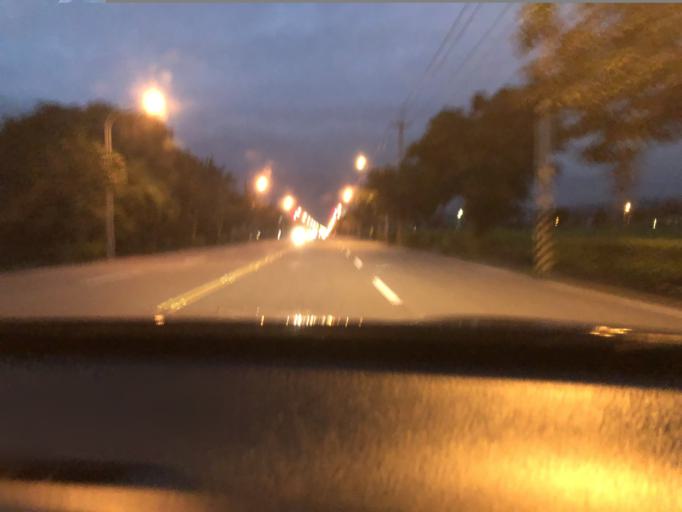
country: TW
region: Taiwan
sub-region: Hualien
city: Hualian
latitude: 23.9504
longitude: 121.5625
